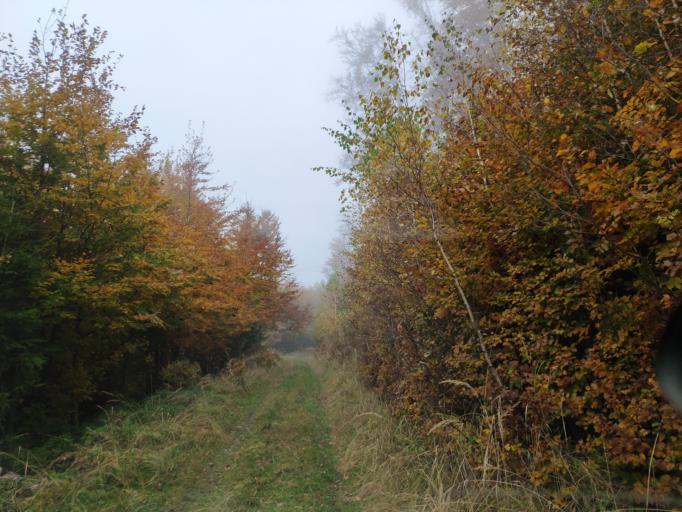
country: SK
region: Kosicky
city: Medzev
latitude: 48.7357
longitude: 20.9940
